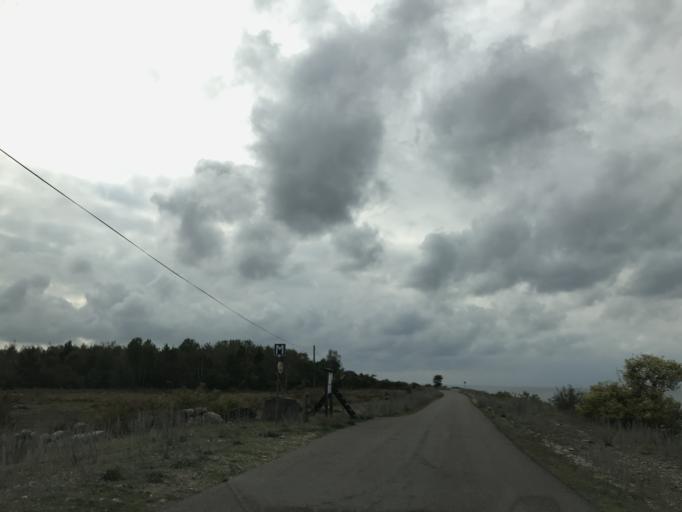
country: SE
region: Kalmar
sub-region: Borgholms Kommun
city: Borgholm
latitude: 57.0616
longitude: 16.8410
